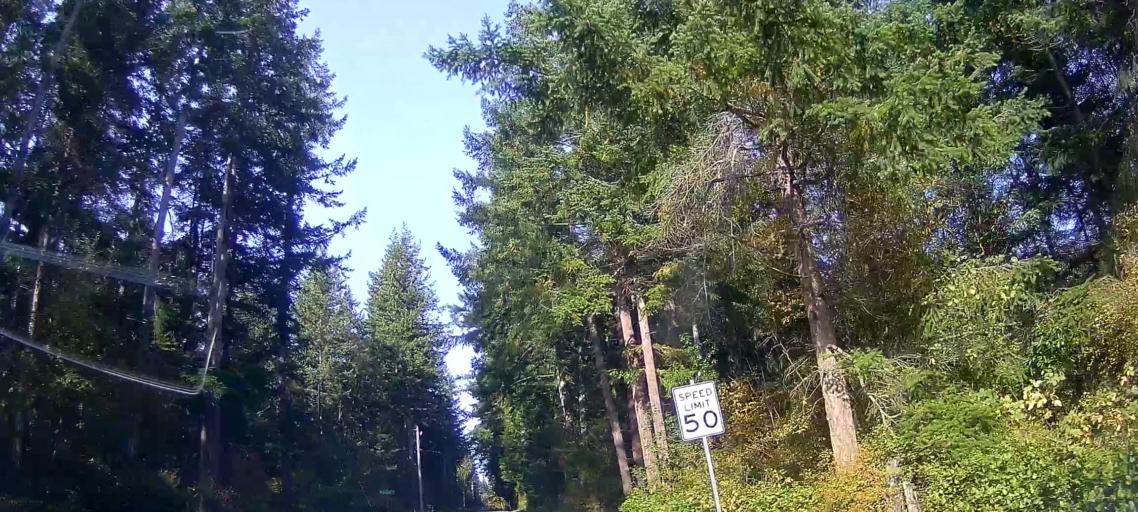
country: US
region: Washington
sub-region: Island County
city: Camano
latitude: 48.2191
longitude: -122.4560
